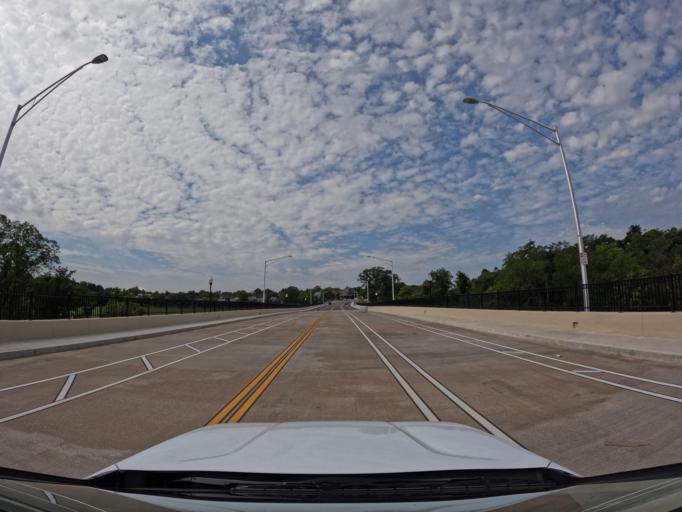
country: US
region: Maryland
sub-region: Baltimore County
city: Parkville
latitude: 39.3346
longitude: -76.5767
